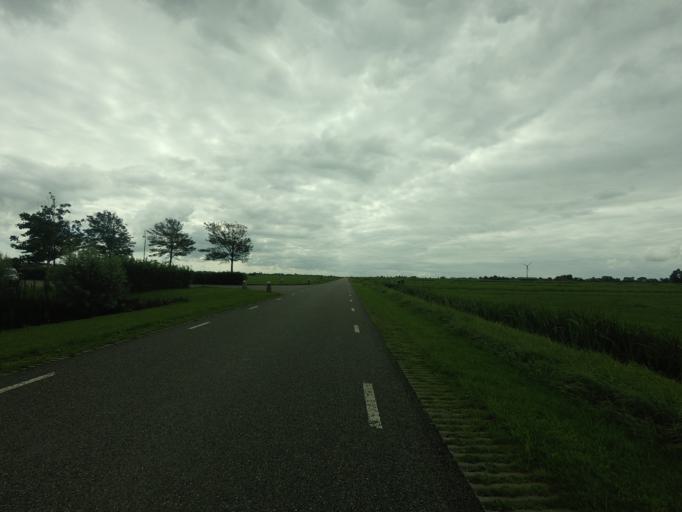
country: NL
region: Friesland
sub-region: Sudwest Fryslan
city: IJlst
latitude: 53.0022
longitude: 5.6353
